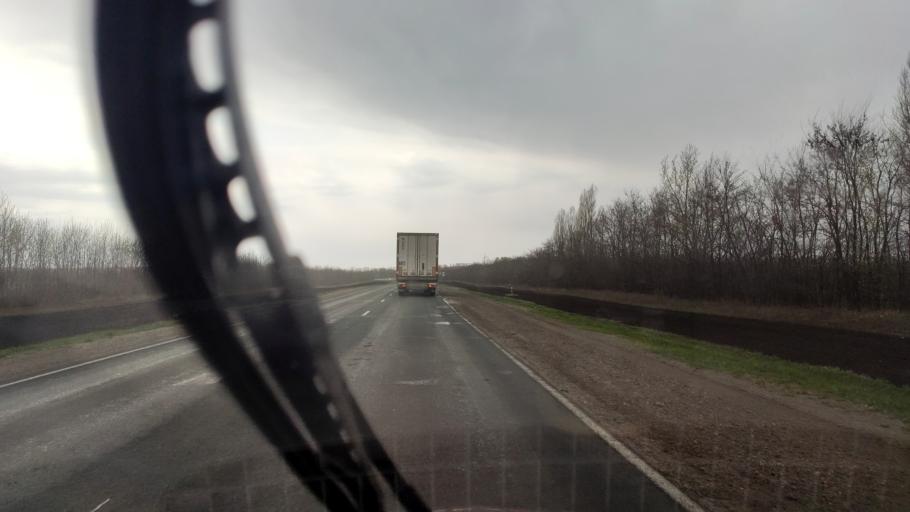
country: RU
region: Voronezj
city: Nizhnedevitsk
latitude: 51.5705
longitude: 38.3349
